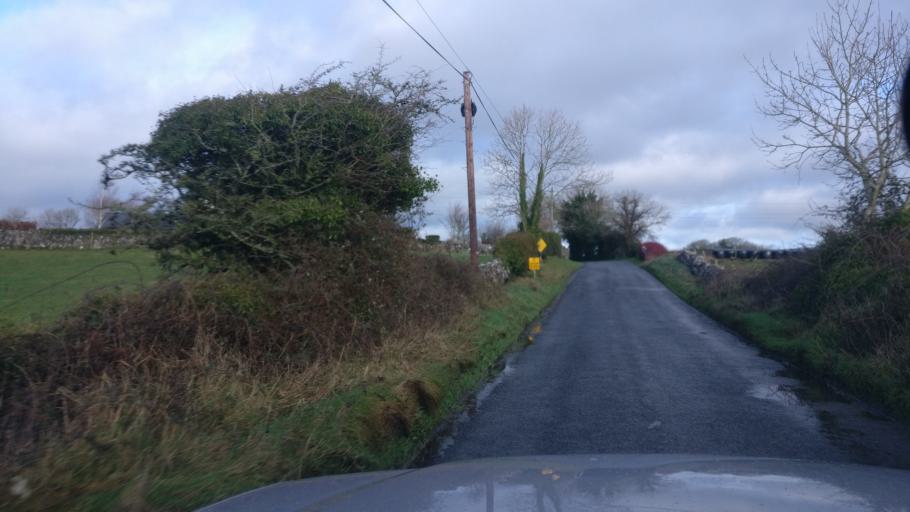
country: IE
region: Connaught
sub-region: County Galway
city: Loughrea
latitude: 53.2150
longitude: -8.5446
